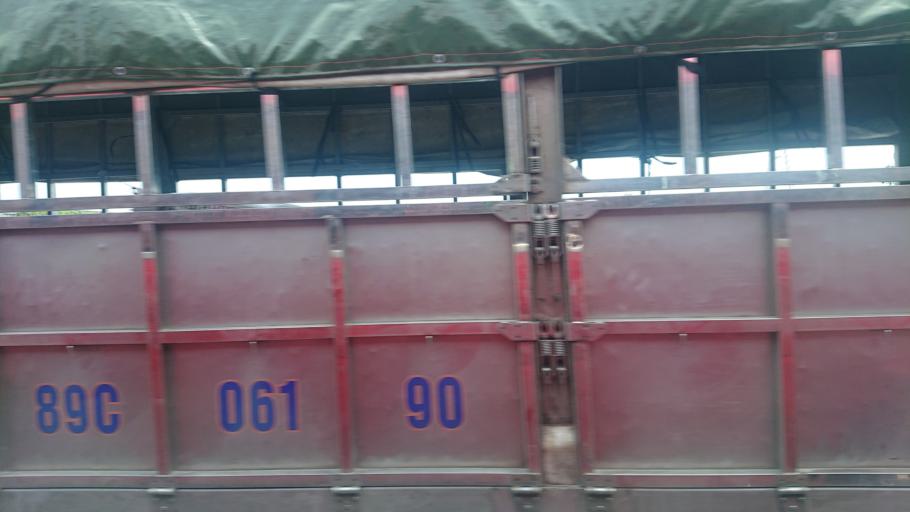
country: VN
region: Hai Phong
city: An Lao
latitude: 20.8023
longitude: 106.5279
